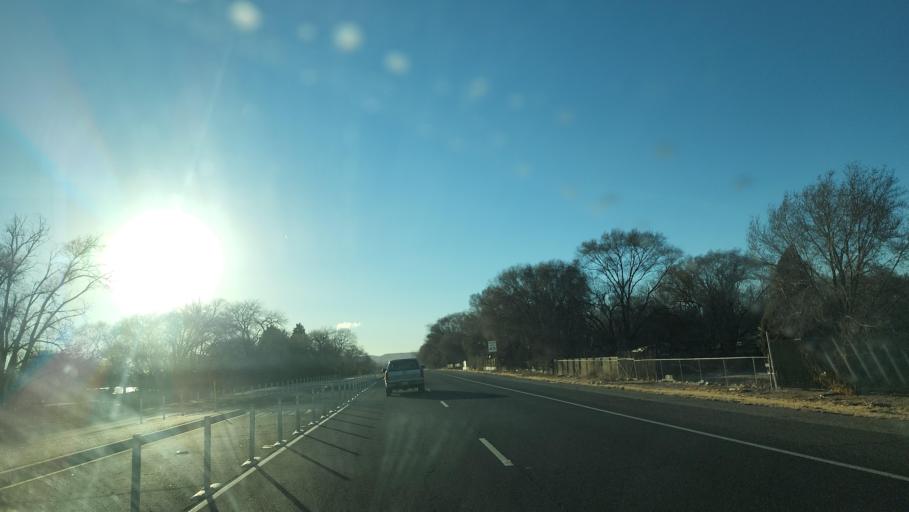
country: US
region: New Mexico
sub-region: Bernalillo County
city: South Valley
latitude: 35.0269
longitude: -106.6912
